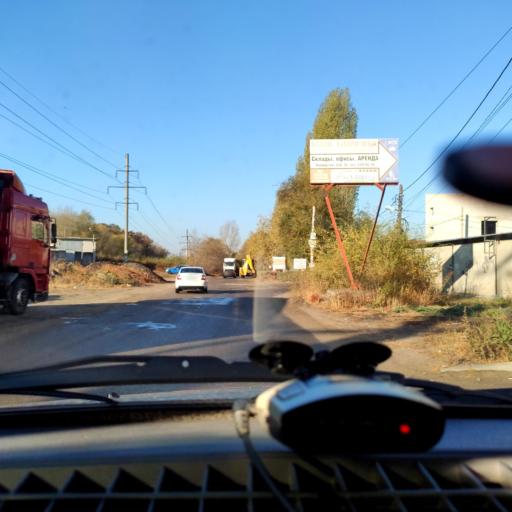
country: RU
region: Voronezj
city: Voronezh
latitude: 51.6689
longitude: 39.1457
